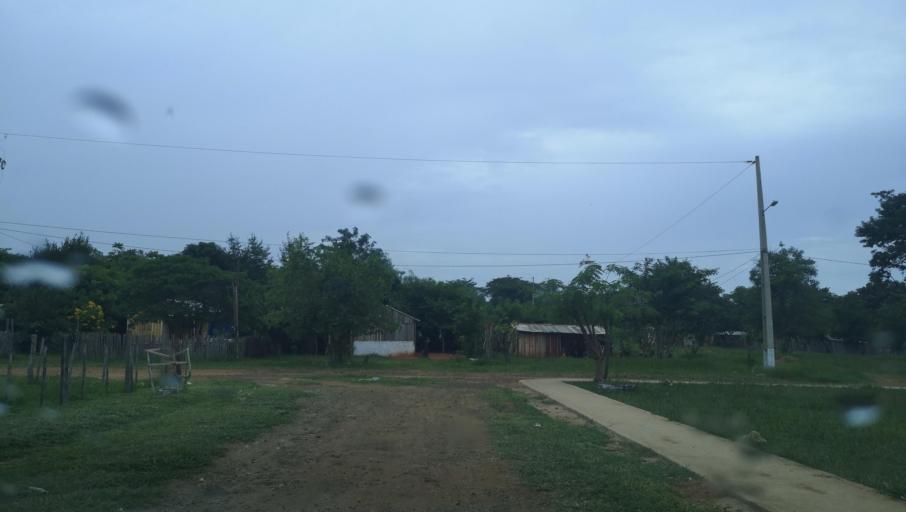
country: PY
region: San Pedro
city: Capiibary
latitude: -24.7256
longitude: -56.0095
